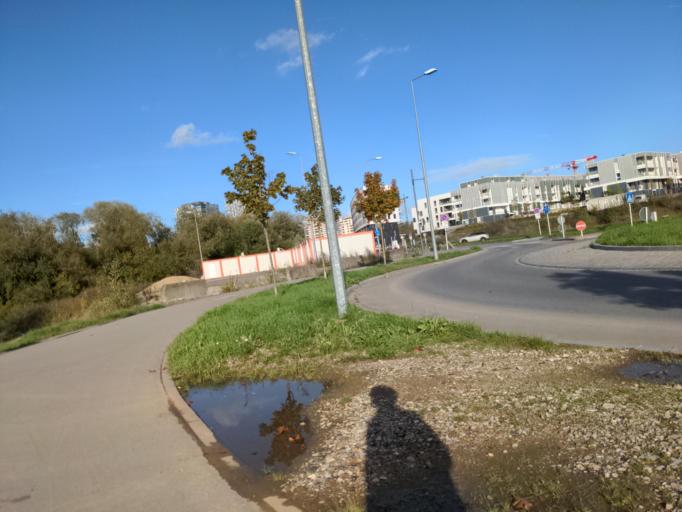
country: LU
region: Luxembourg
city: Kirchberg
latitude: 49.6336
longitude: 6.1581
